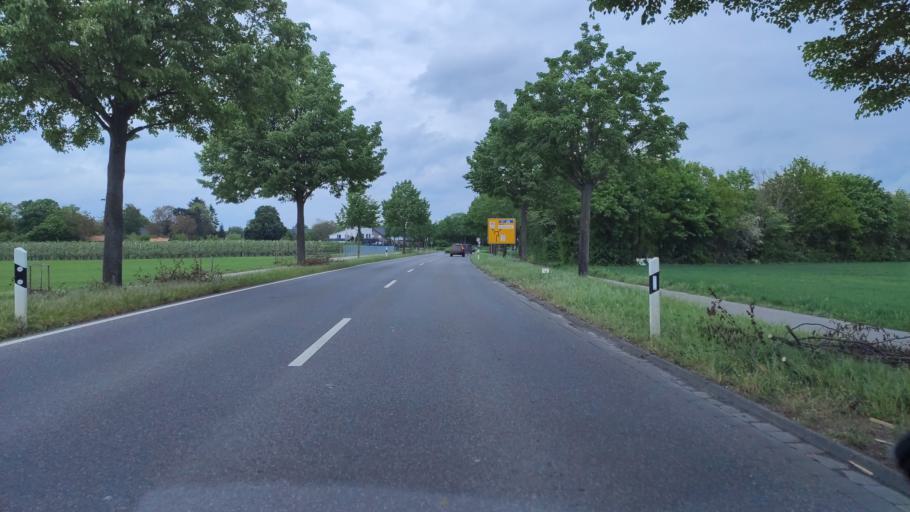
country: DE
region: North Rhine-Westphalia
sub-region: Regierungsbezirk Dusseldorf
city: Kaarst
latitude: 51.2093
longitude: 6.6207
